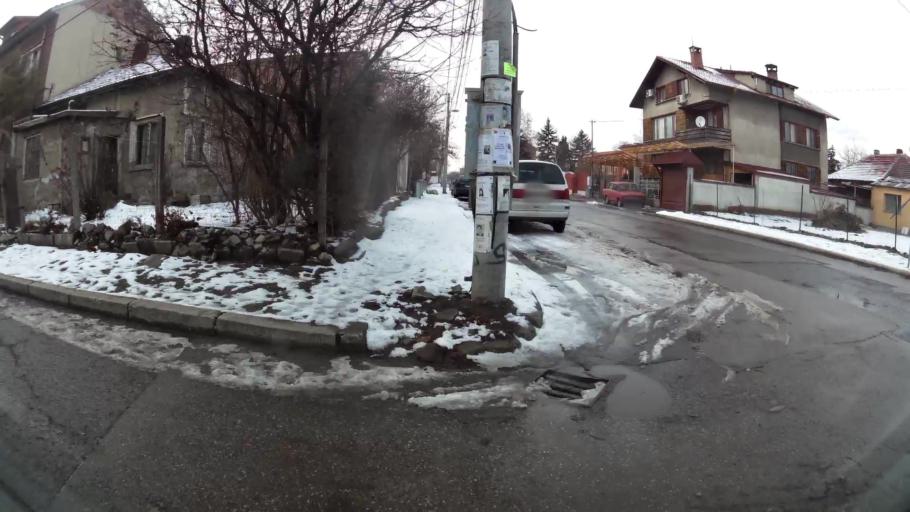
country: BG
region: Sofia-Capital
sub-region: Stolichna Obshtina
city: Sofia
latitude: 42.7229
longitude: 23.3326
